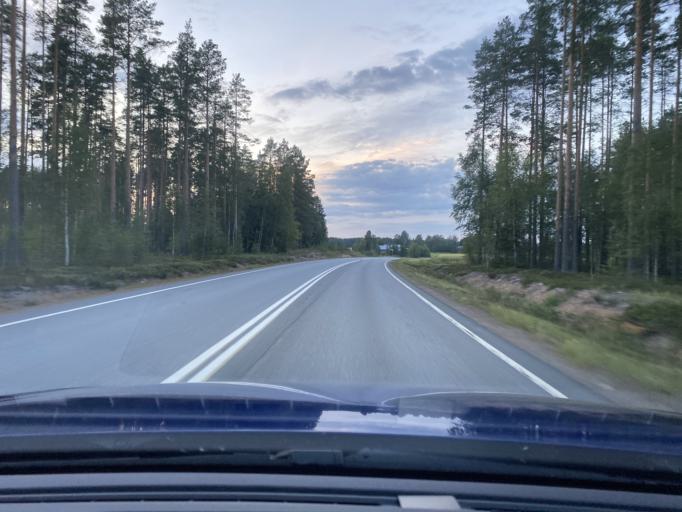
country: FI
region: Satakunta
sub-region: Pohjois-Satakunta
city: Honkajoki
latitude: 62.0952
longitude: 22.2436
